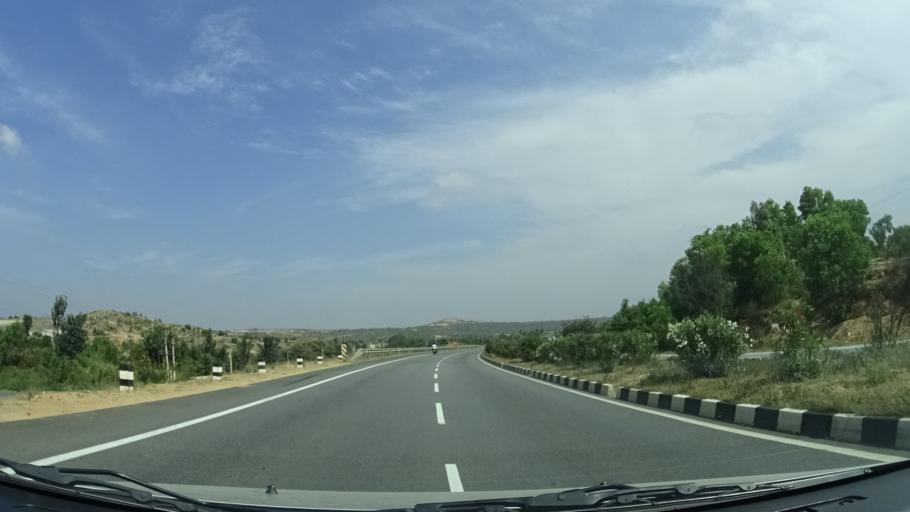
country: IN
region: Karnataka
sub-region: Chikkaballapur
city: Chik Ballapur
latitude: 13.5311
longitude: 77.7655
